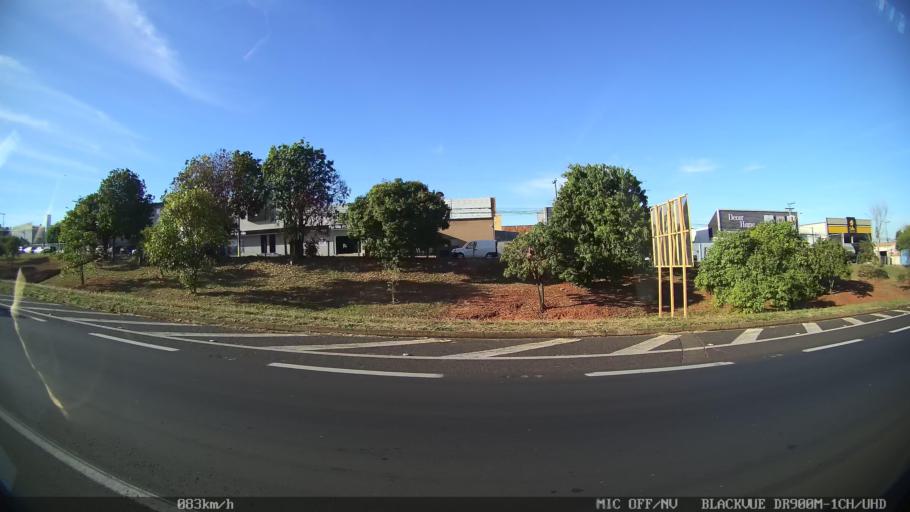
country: BR
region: Sao Paulo
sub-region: Sao Jose Do Rio Preto
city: Sao Jose do Rio Preto
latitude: -20.8396
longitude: -49.3537
